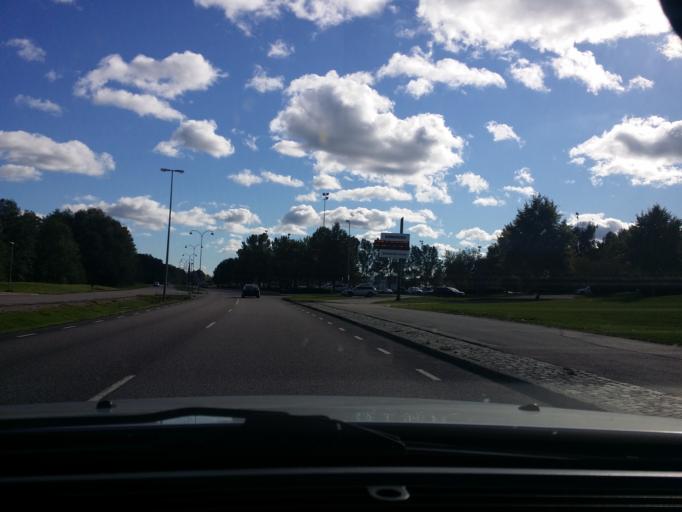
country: SE
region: Vaestmanland
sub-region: Vasteras
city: Vasteras
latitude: 59.6329
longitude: 16.5317
